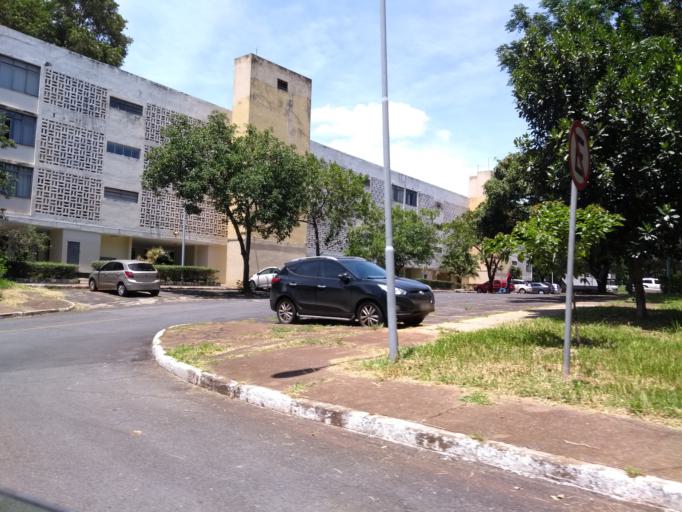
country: BR
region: Federal District
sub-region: Brasilia
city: Brasilia
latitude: -15.8330
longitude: -47.9146
